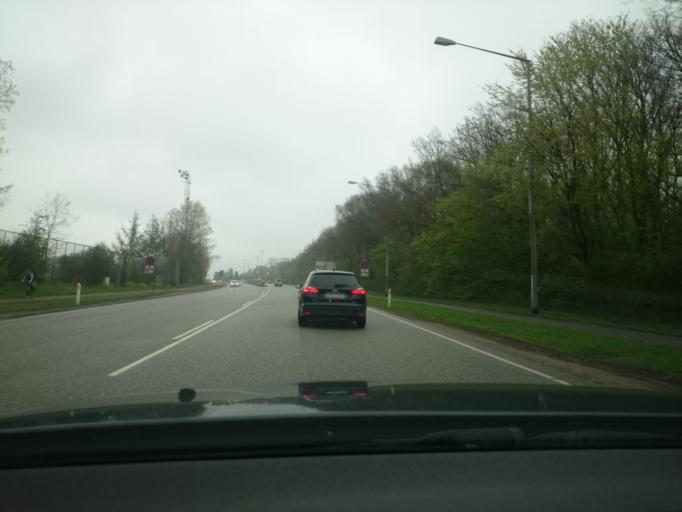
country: DK
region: Capital Region
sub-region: Herlev Kommune
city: Herlev
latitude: 55.7604
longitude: 12.4343
